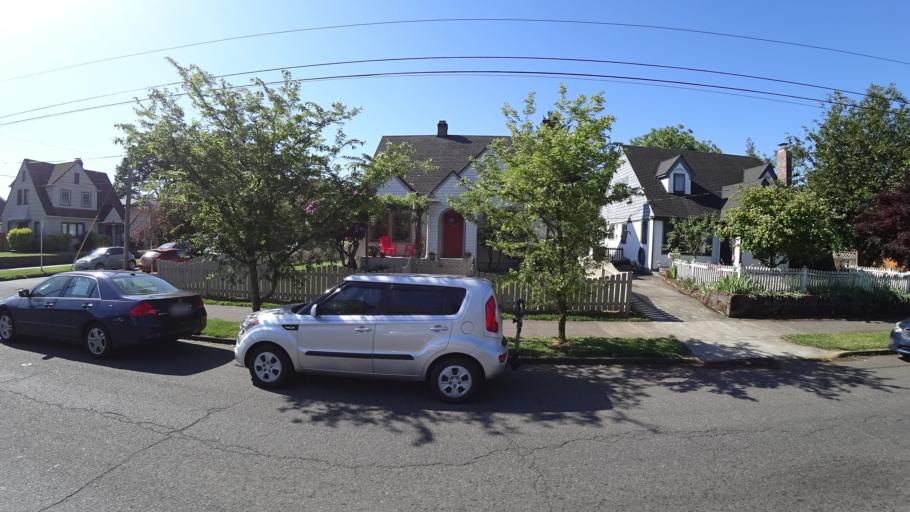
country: US
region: Oregon
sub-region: Multnomah County
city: Portland
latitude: 45.5483
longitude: -122.6129
